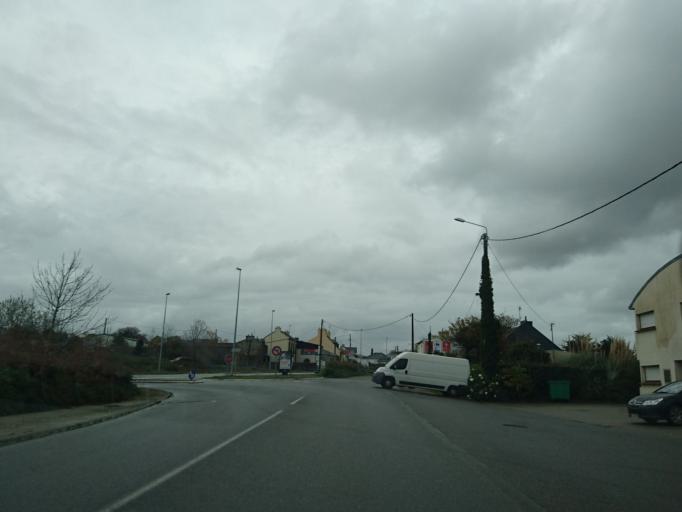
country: FR
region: Brittany
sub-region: Departement du Finistere
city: Plougonvelin
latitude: 48.3614
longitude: -4.6745
